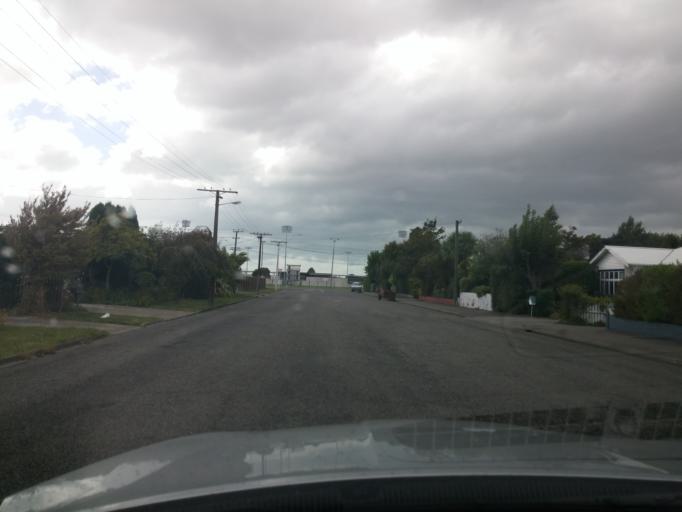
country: NZ
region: Marlborough
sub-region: Marlborough District
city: Blenheim
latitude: -41.4991
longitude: 173.9530
